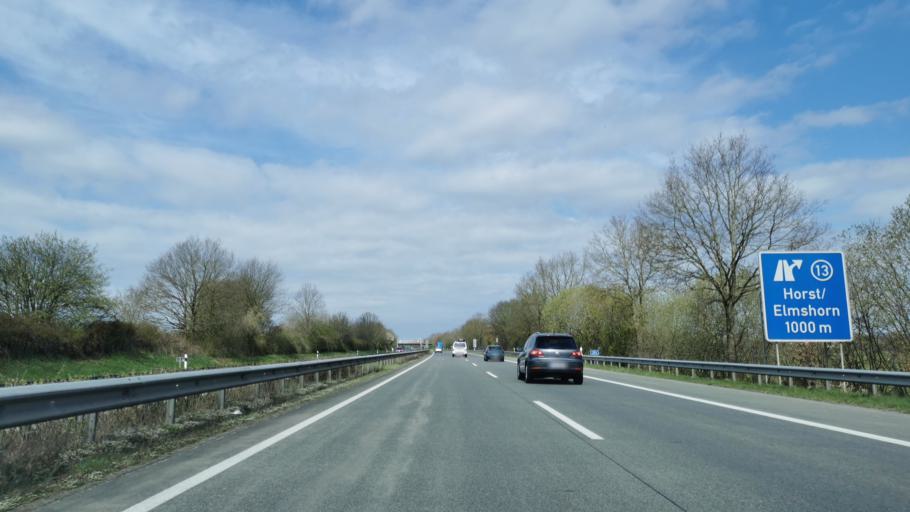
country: DE
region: Schleswig-Holstein
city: Klein Offenseth-Sparrieshoop
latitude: 53.7967
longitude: 9.6921
